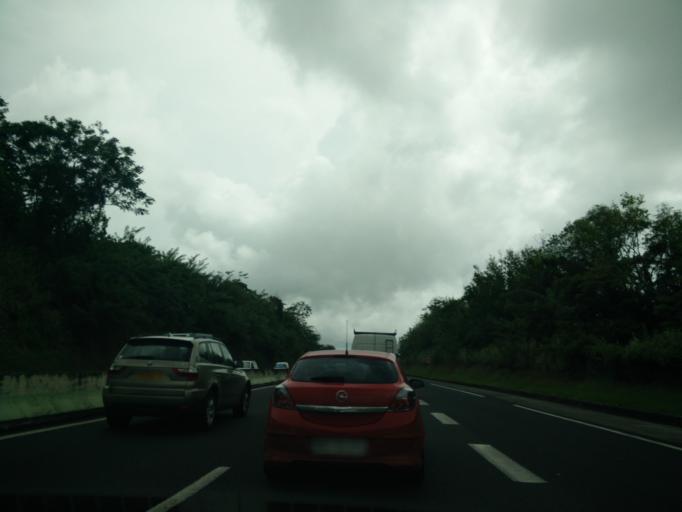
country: MQ
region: Martinique
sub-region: Martinique
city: Ducos
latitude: 14.5805
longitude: -60.9813
